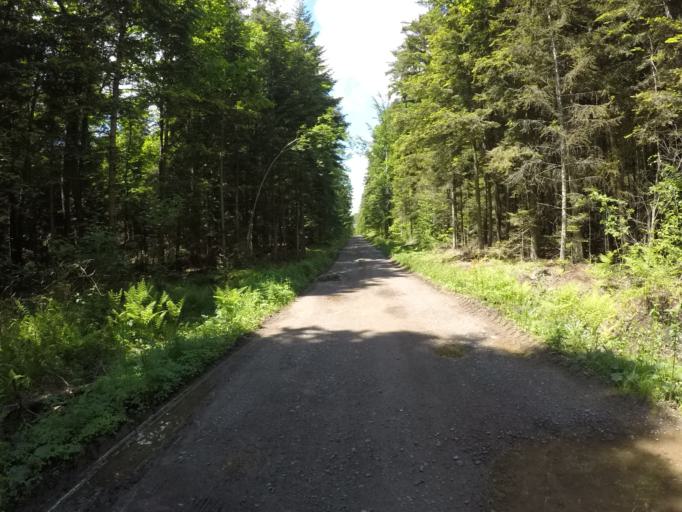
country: PL
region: Swietokrzyskie
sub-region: Powiat kielecki
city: Kostomloty Pierwsze
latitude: 50.9178
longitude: 20.6399
